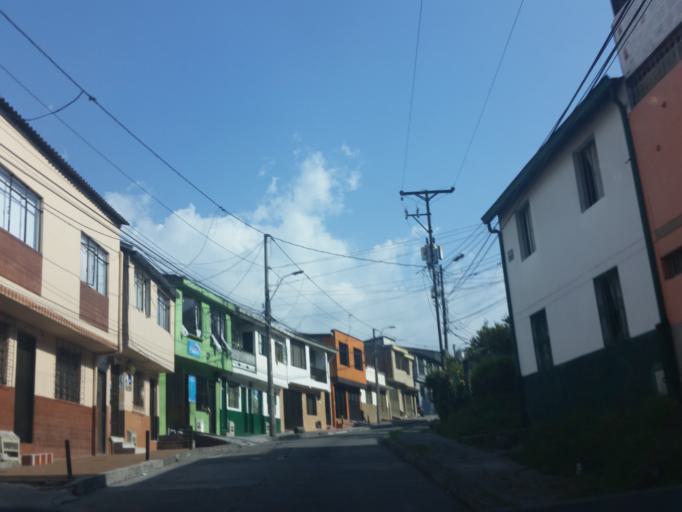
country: CO
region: Caldas
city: Manizales
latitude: 5.0687
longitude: -75.4957
